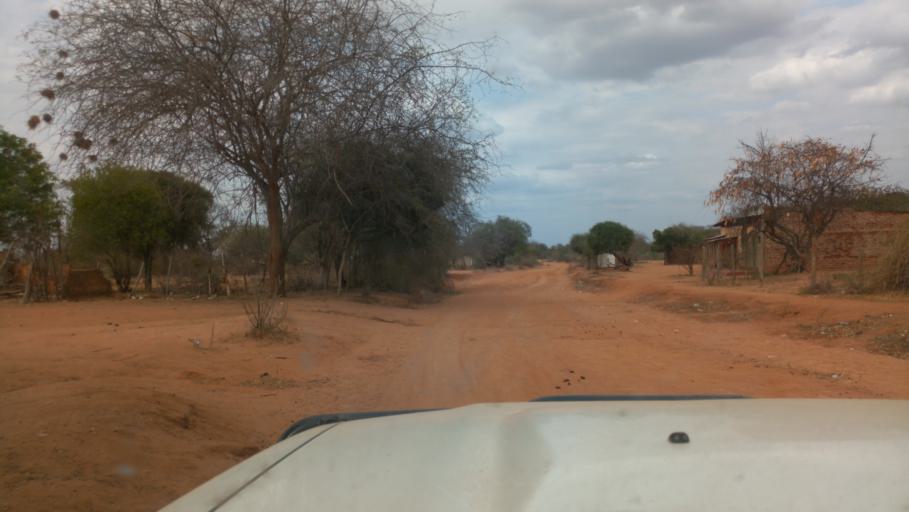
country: KE
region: Kitui
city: Kitui
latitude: -1.7969
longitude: 38.4452
